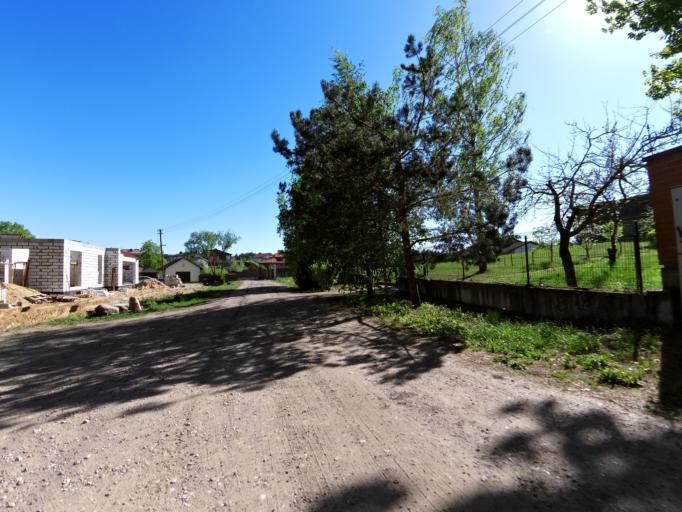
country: LT
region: Vilnius County
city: Pilaite
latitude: 54.6975
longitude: 25.1637
